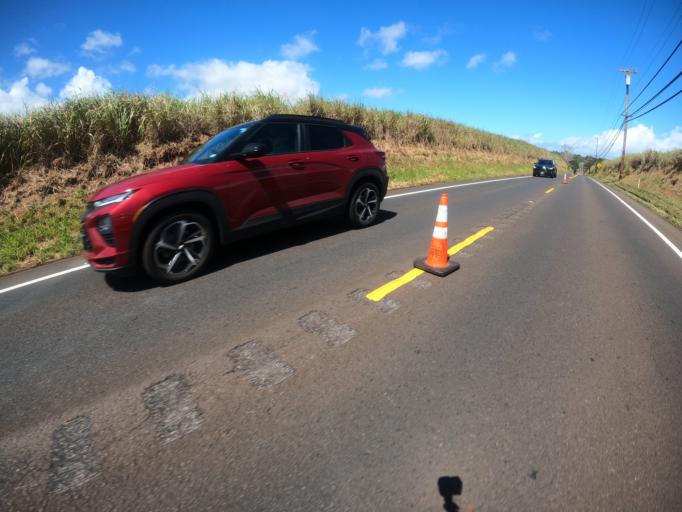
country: US
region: Hawaii
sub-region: Honolulu County
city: Schofield Barracks
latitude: 21.4721
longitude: -158.0524
